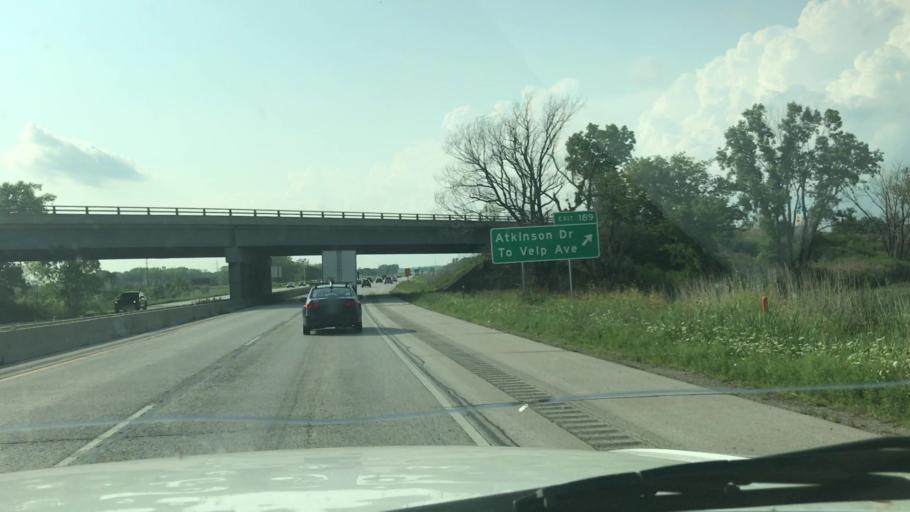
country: US
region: Wisconsin
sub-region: Brown County
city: Green Bay
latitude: 44.5403
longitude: -88.0245
